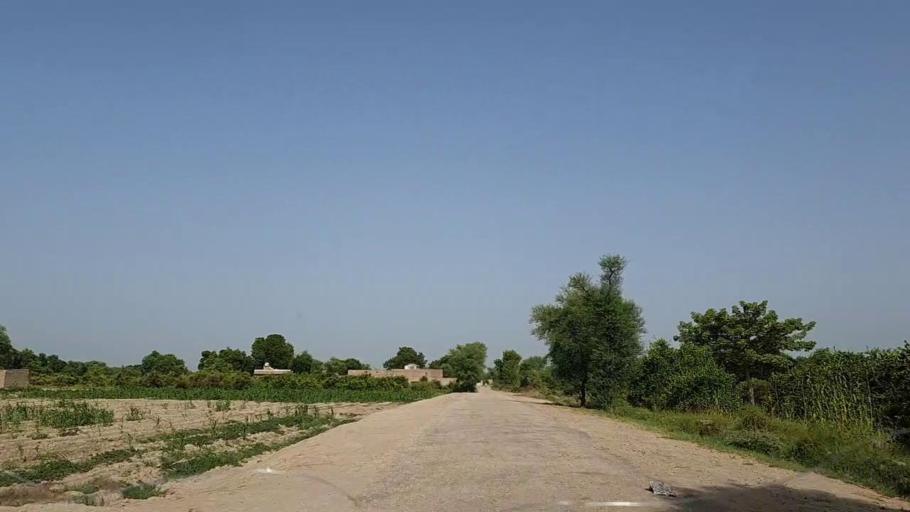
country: PK
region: Sindh
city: Kandiaro
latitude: 27.0715
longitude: 68.1563
